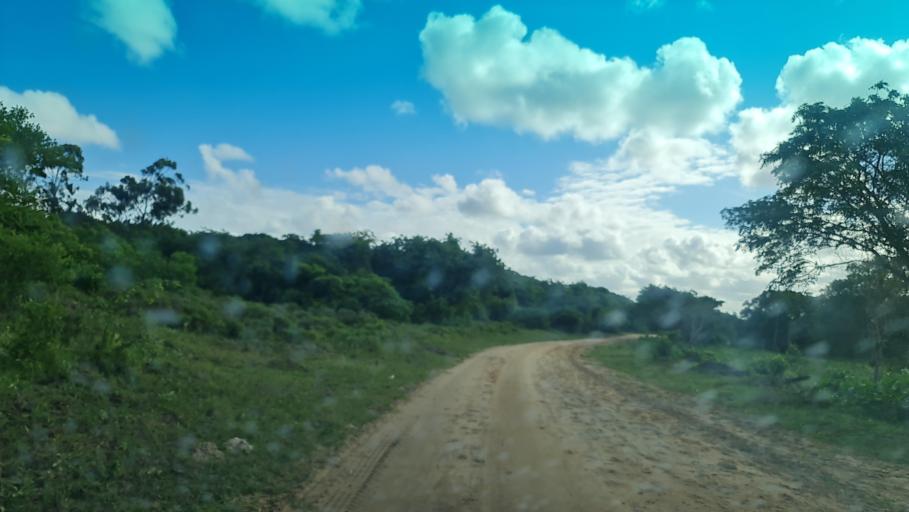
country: MZ
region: Maputo
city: Manhica
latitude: -25.4361
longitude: 32.8834
